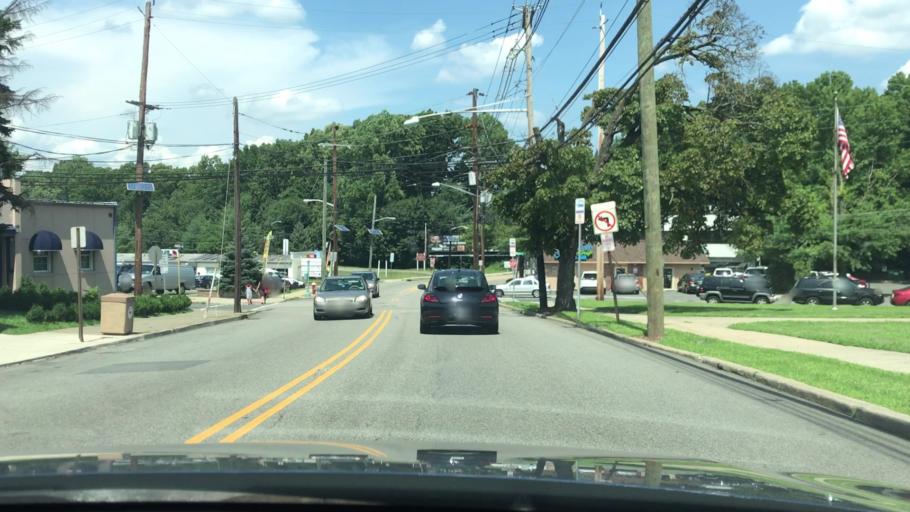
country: US
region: New Jersey
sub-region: Passaic County
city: Clifton
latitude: 40.8686
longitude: -74.1556
